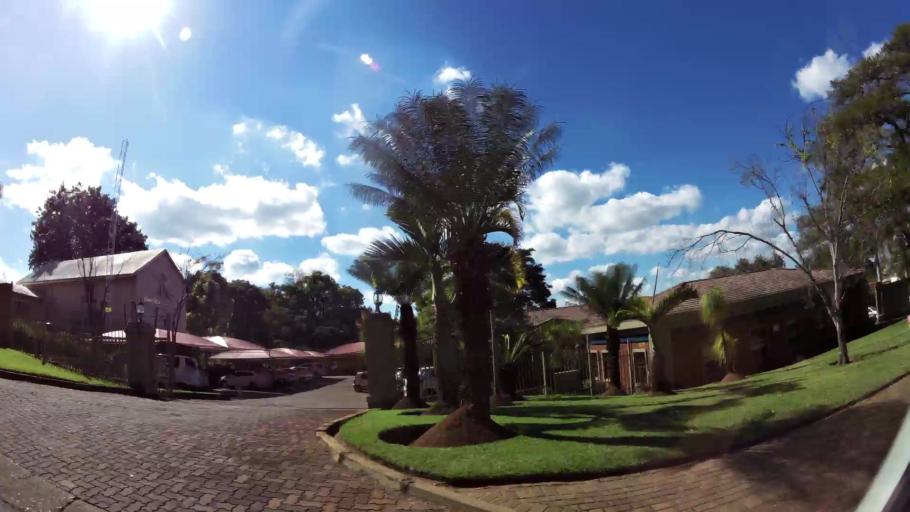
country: ZA
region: Limpopo
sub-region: Mopani District Municipality
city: Tzaneen
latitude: -23.8317
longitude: 30.1573
